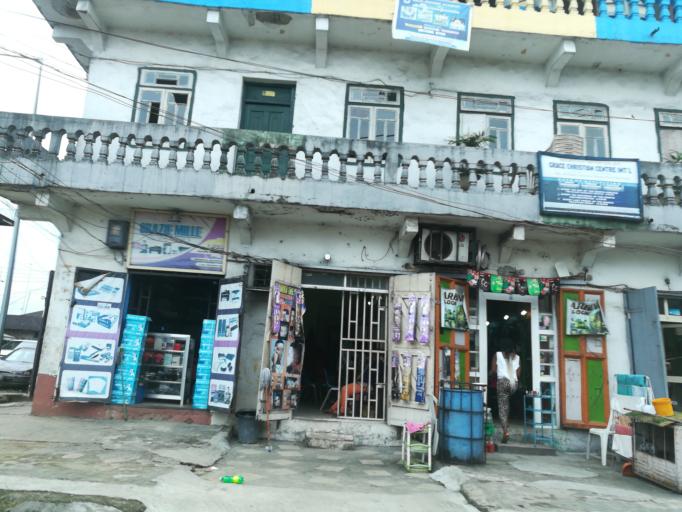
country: NG
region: Rivers
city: Port Harcourt
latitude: 4.7654
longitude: 7.0203
